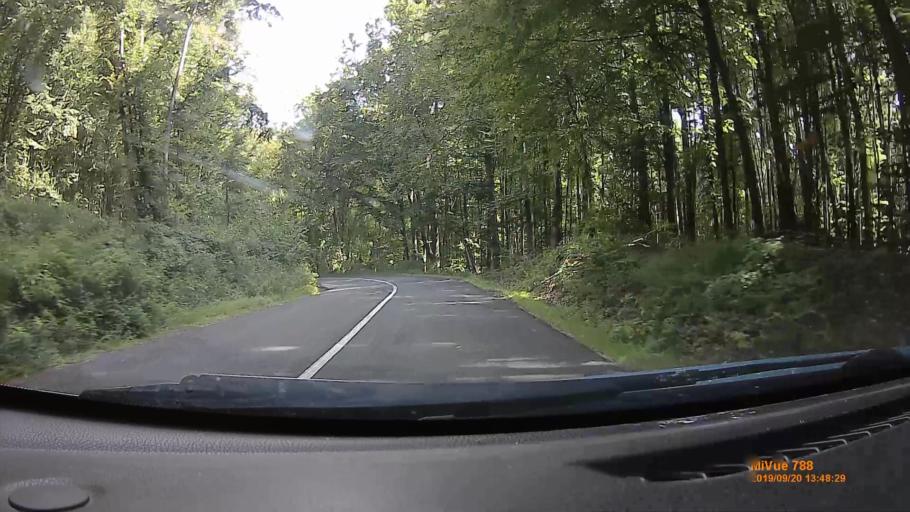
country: HU
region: Borsod-Abauj-Zemplen
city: Saly
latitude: 48.0646
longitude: 20.5831
